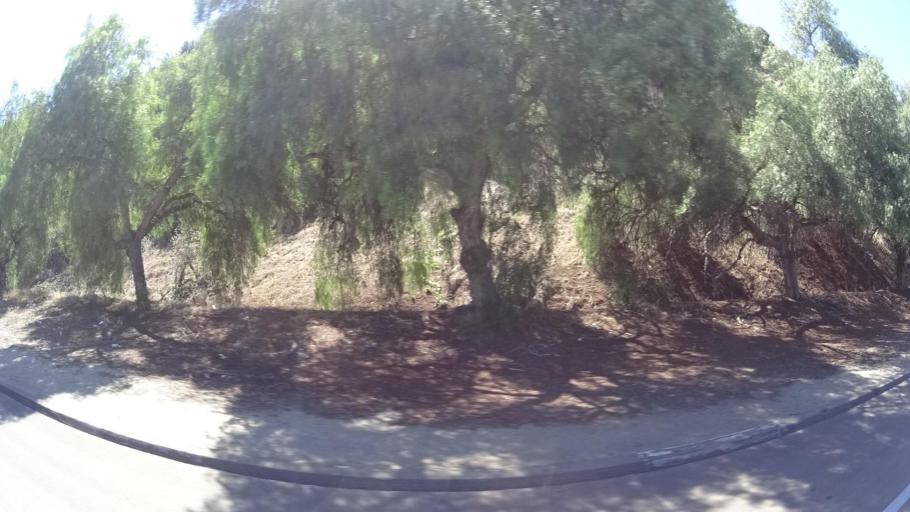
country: US
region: California
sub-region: San Diego County
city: Fairbanks Ranch
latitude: 32.9751
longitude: -117.2201
